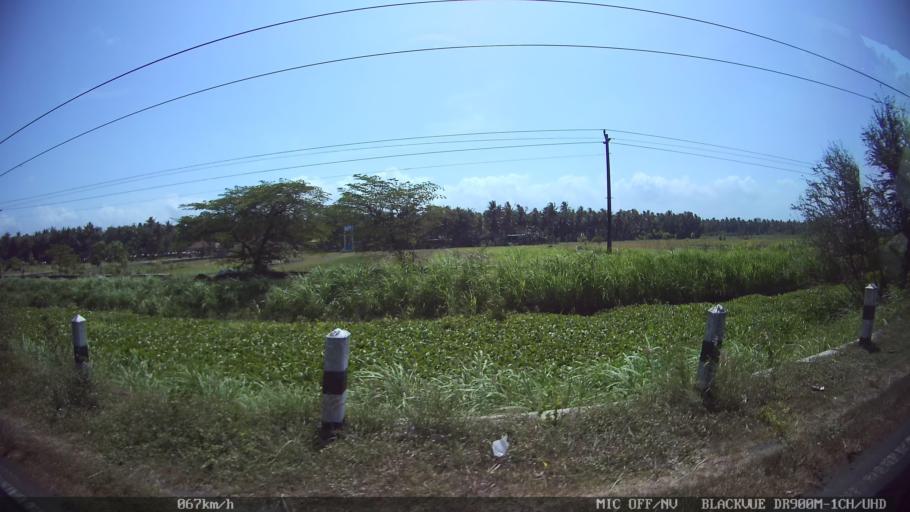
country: ID
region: Daerah Istimewa Yogyakarta
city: Srandakan
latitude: -7.9423
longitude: 110.1671
